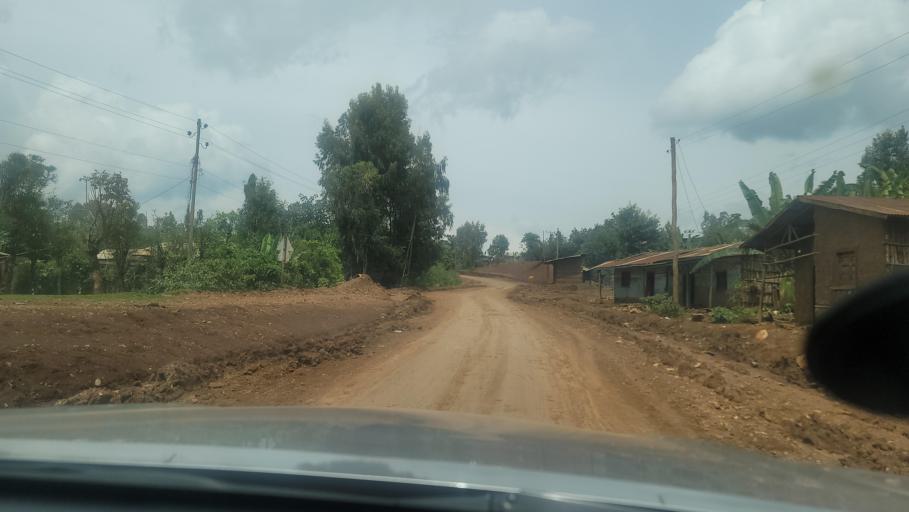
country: ET
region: Oromiya
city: Agaro
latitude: 7.8255
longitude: 36.5406
